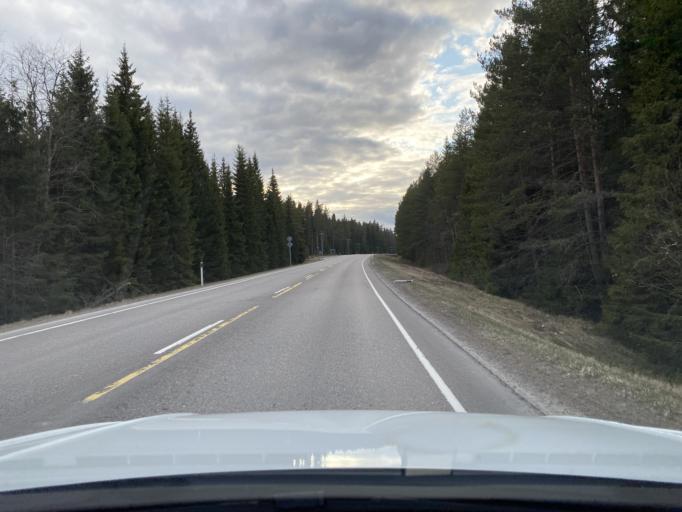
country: FI
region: Haeme
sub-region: Riihimaeki
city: Loppi
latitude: 60.7500
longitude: 24.3163
